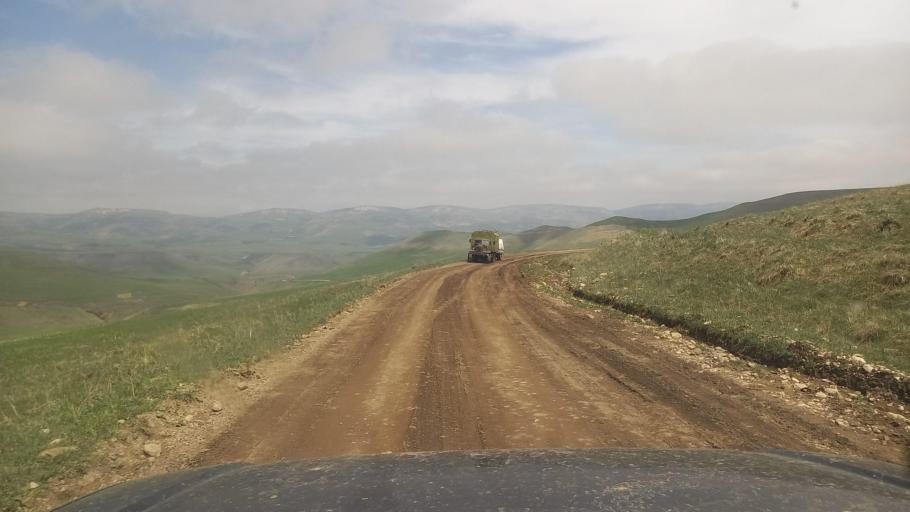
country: RU
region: Stavropol'skiy
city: Kislovodsk
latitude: 43.7793
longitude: 42.8560
